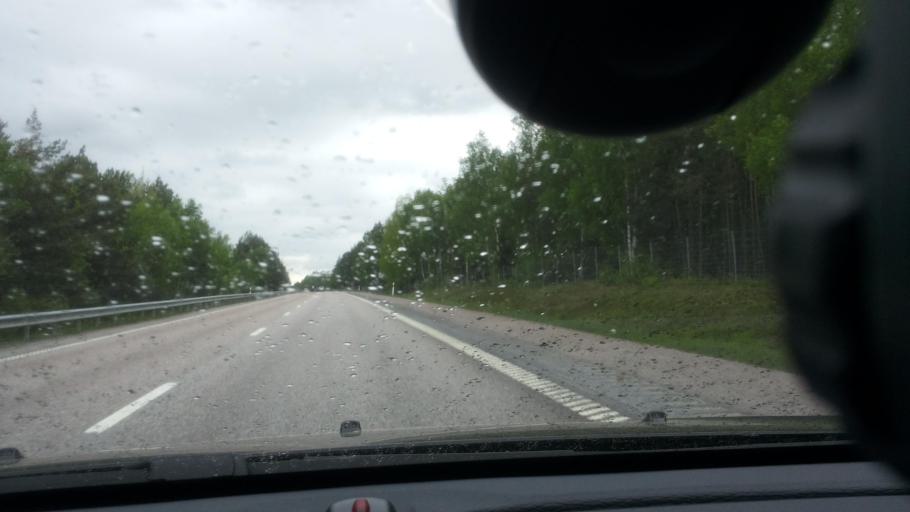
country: SE
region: Stockholm
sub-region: Sigtuna Kommun
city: Marsta
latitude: 59.6487
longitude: 17.8912
